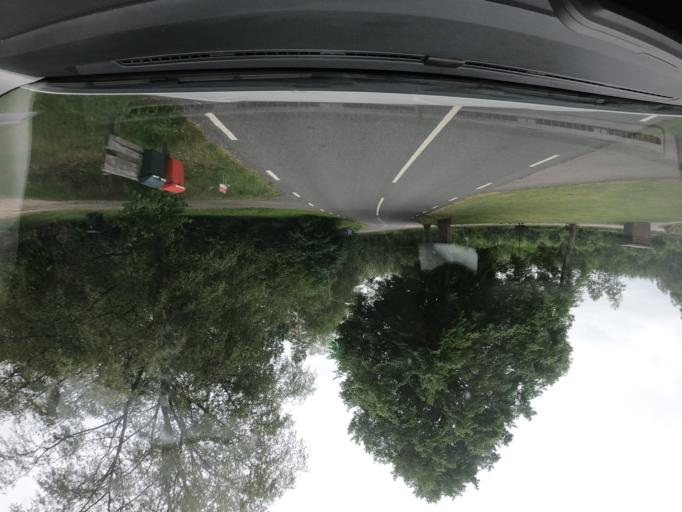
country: SE
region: Skane
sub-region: Perstorps Kommun
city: Perstorp
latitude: 56.1455
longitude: 13.3488
